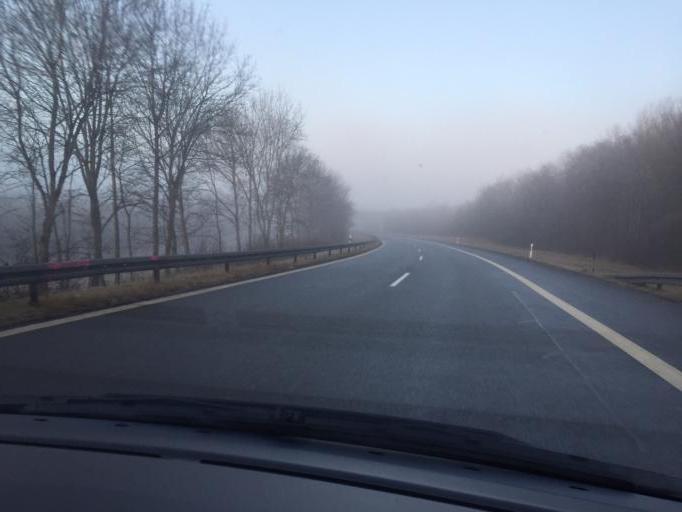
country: DE
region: Baden-Wuerttemberg
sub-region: Freiburg Region
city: Tuningen
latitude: 47.9941
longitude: 8.6054
